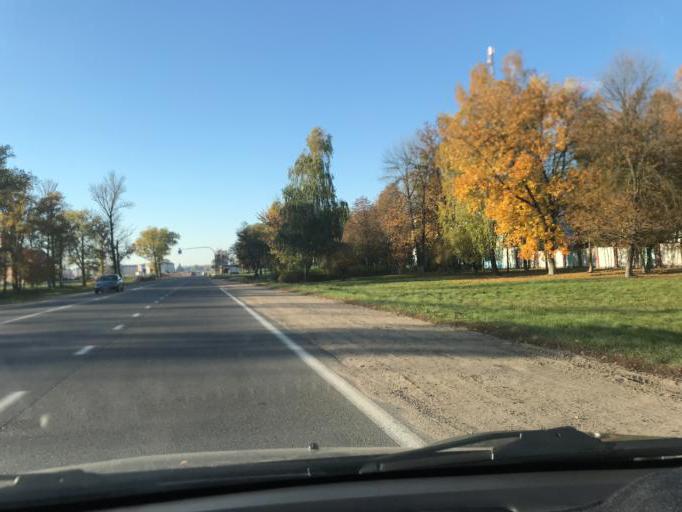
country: BY
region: Minsk
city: Slutsk
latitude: 53.0416
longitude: 27.5819
